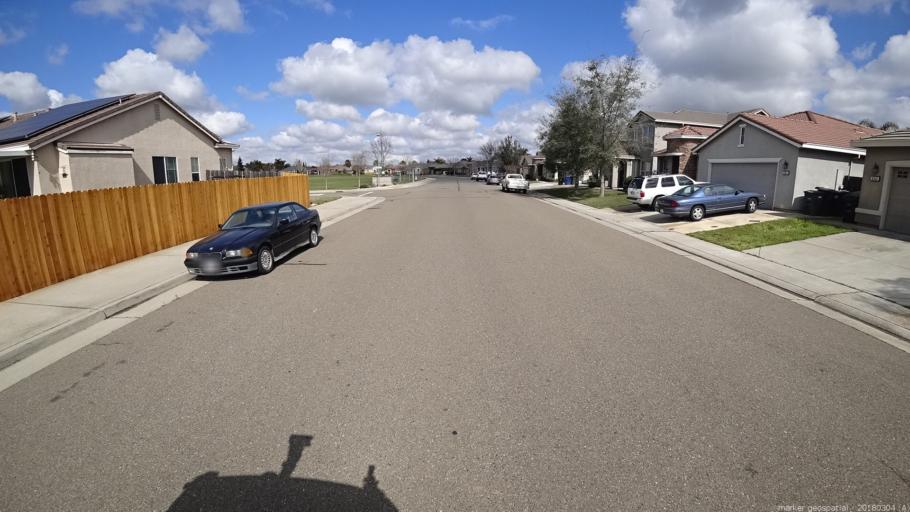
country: US
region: California
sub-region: Sacramento County
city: Vineyard
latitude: 38.4554
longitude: -121.3241
